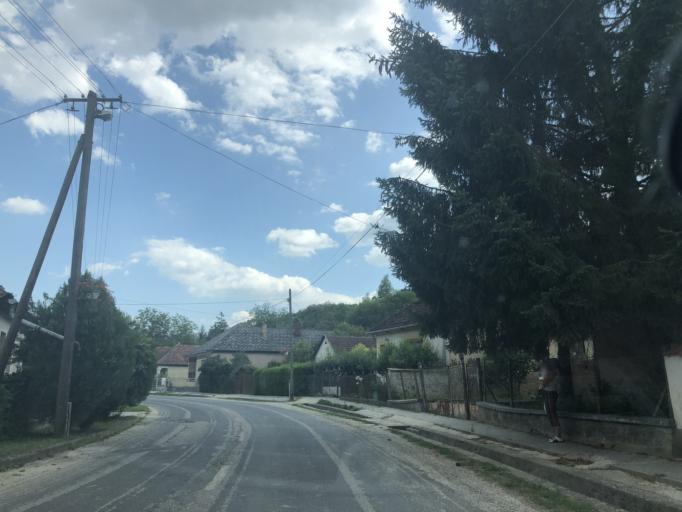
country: HU
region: Borsod-Abauj-Zemplen
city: Szendro
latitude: 48.4406
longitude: 20.7939
